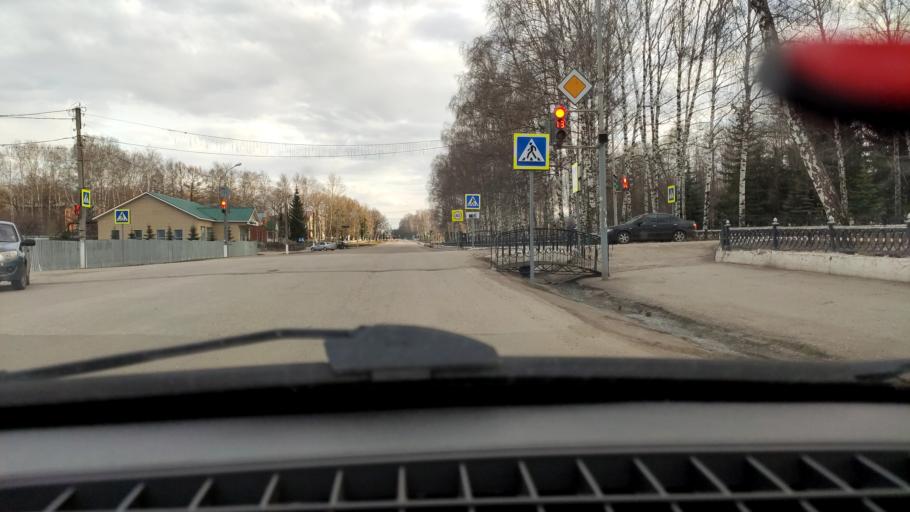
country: RU
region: Bashkortostan
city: Tolbazy
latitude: 54.0163
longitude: 55.8864
